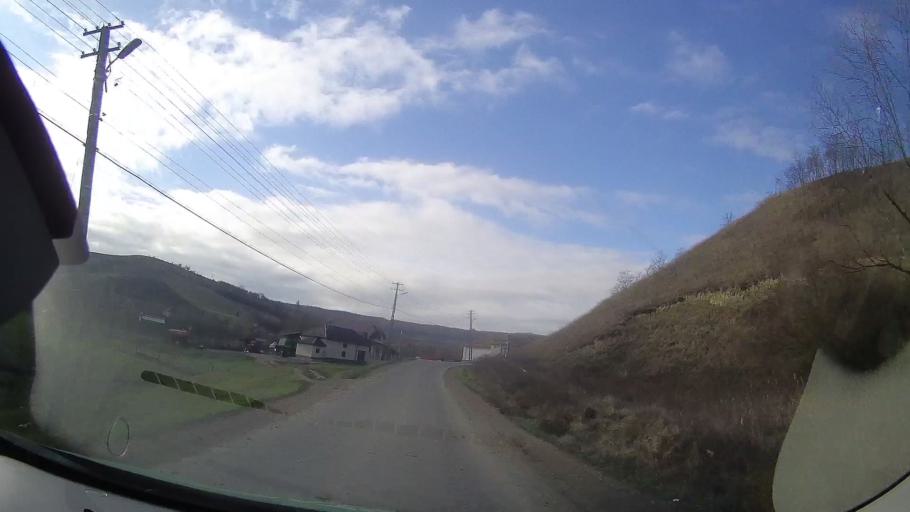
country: RO
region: Mures
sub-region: Comuna Papiu Ilarian
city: Papiu Ilarian
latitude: 46.5602
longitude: 24.2045
